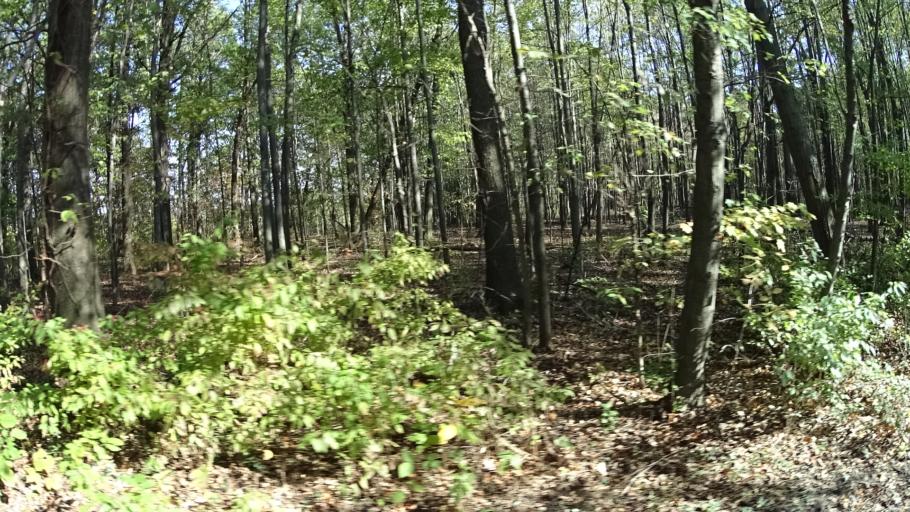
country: US
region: Ohio
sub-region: Lorain County
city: Vermilion
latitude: 41.4121
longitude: -82.3463
